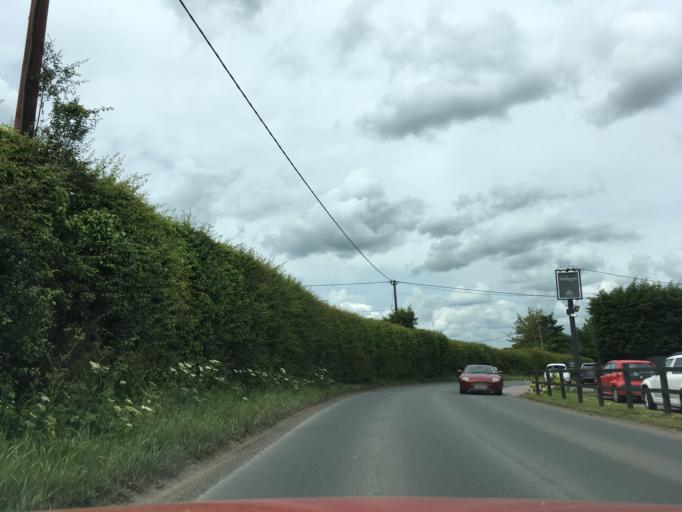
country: GB
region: England
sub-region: Wiltshire
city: Royal Wootton Bassett
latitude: 51.5650
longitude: -1.8896
